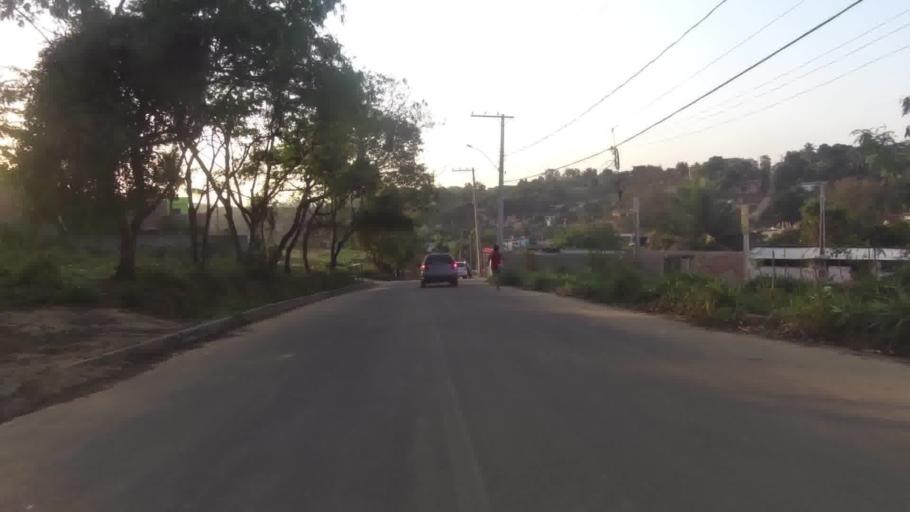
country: BR
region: Espirito Santo
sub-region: Piuma
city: Piuma
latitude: -20.8311
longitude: -40.7205
